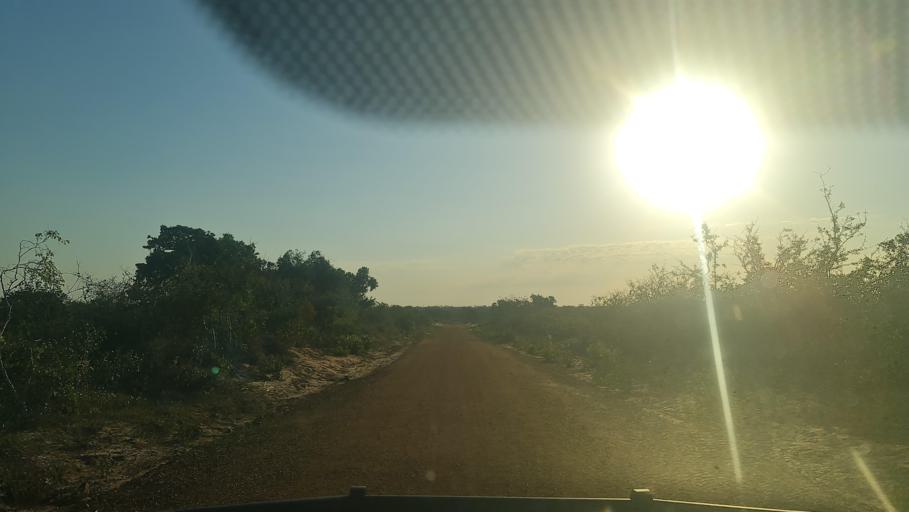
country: MZ
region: Nampula
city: Antonio Enes
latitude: -15.7076
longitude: 40.2544
